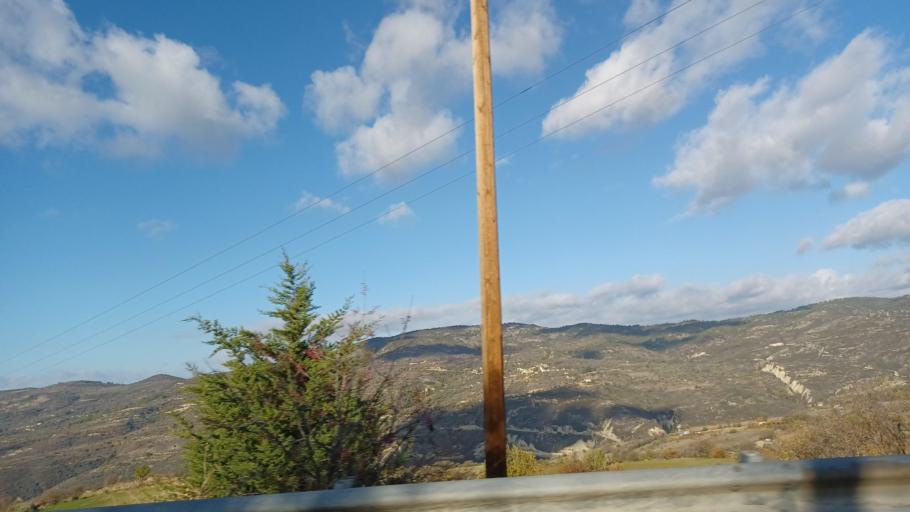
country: CY
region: Limassol
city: Pachna
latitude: 34.8495
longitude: 32.7403
